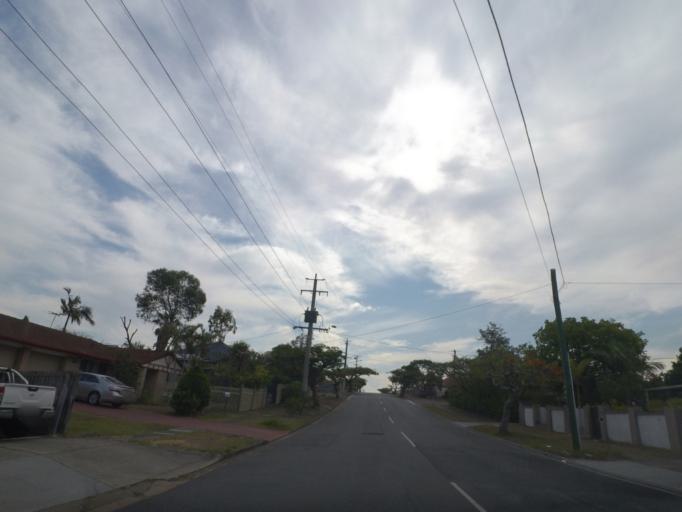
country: AU
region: Queensland
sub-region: Brisbane
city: Inala
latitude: -27.5893
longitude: 152.9745
